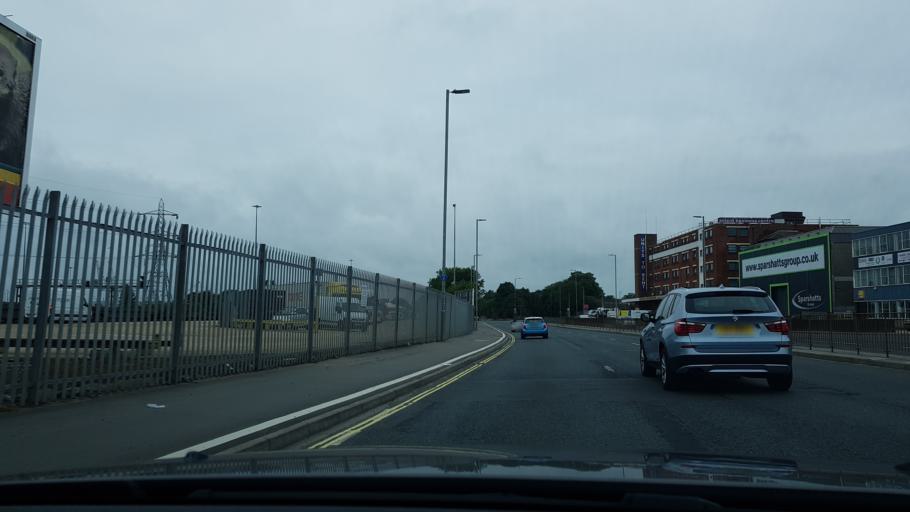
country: GB
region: England
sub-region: Hampshire
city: Marchwood
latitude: 50.9128
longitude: -1.4370
